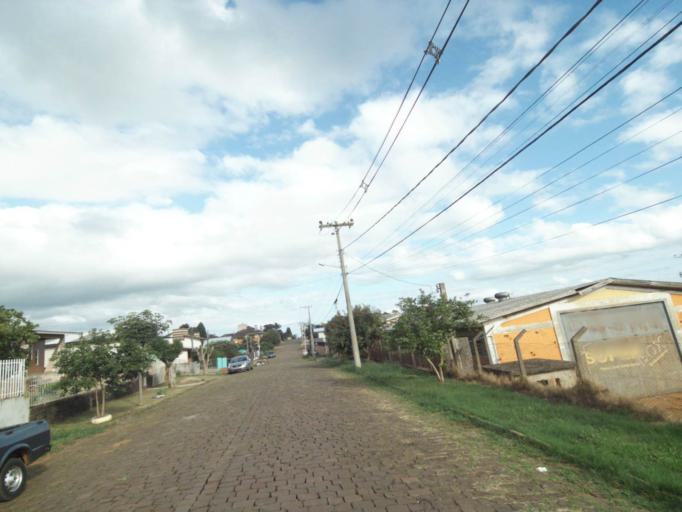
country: BR
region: Rio Grande do Sul
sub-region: Lagoa Vermelha
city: Lagoa Vermelha
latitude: -28.2055
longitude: -51.5177
